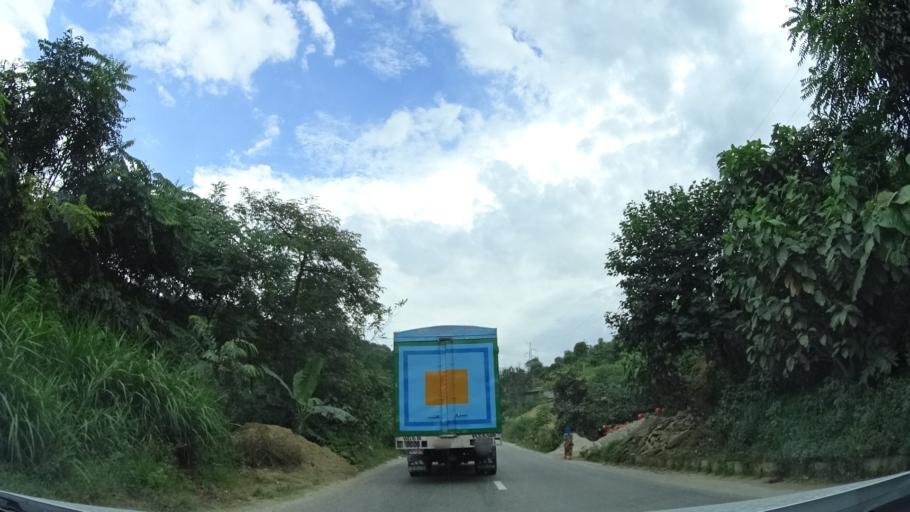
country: NP
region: Central Region
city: Kirtipur
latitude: 27.7470
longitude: 85.0785
